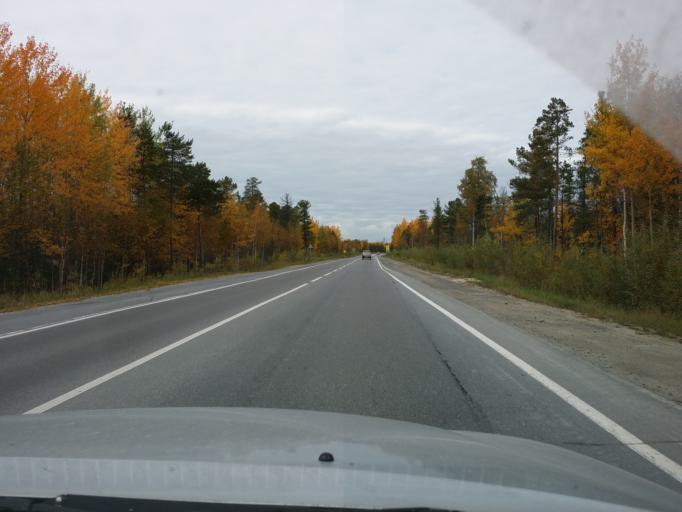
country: RU
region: Khanty-Mansiyskiy Avtonomnyy Okrug
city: Megion
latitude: 61.1305
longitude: 75.7796
